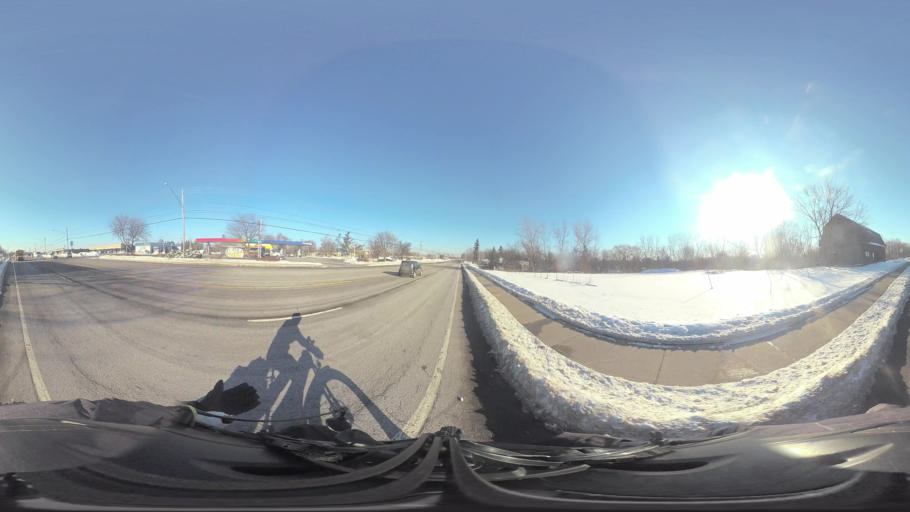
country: US
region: New York
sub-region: Monroe County
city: Rochester
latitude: 43.0713
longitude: -77.6075
